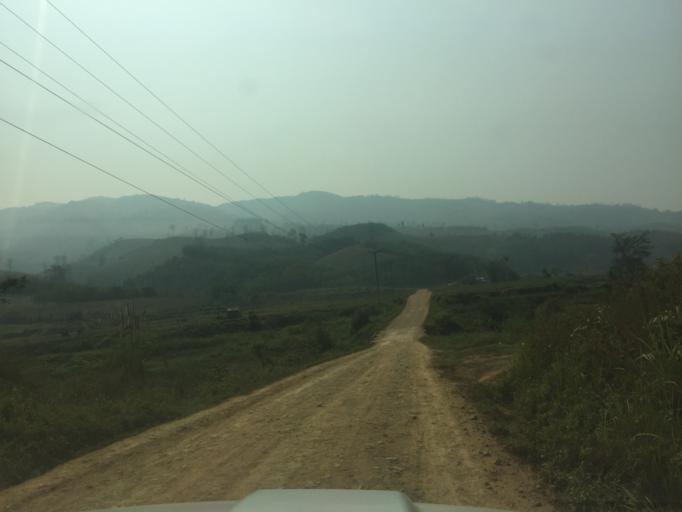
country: TH
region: Phayao
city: Phu Sang
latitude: 19.6708
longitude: 100.5260
